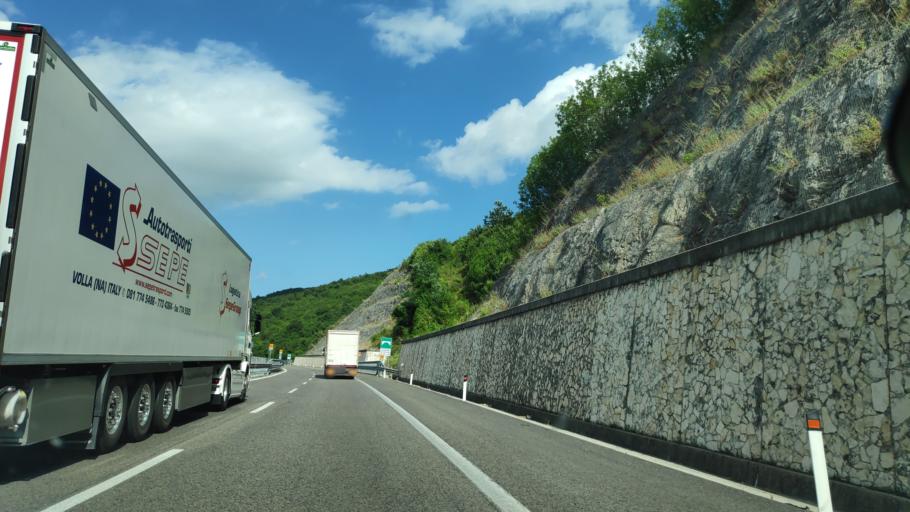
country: IT
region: Campania
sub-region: Provincia di Salerno
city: Pertosa
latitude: 40.5311
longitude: 15.4494
